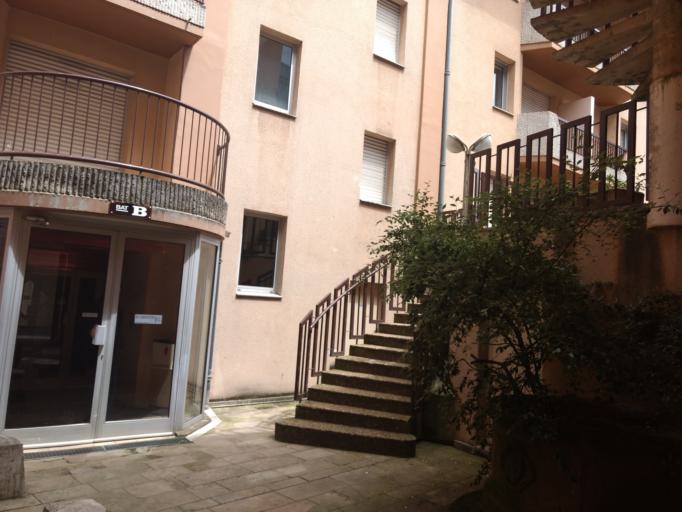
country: FR
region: Midi-Pyrenees
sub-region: Departement de l'Aveyron
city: Rodez
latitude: 44.3507
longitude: 2.5767
